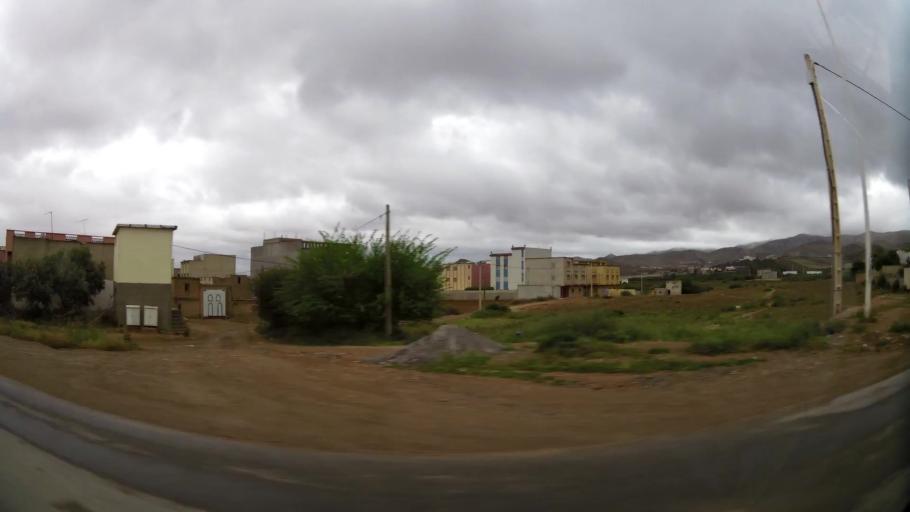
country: MA
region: Oriental
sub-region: Nador
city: Midar
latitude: 35.0542
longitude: -3.4624
